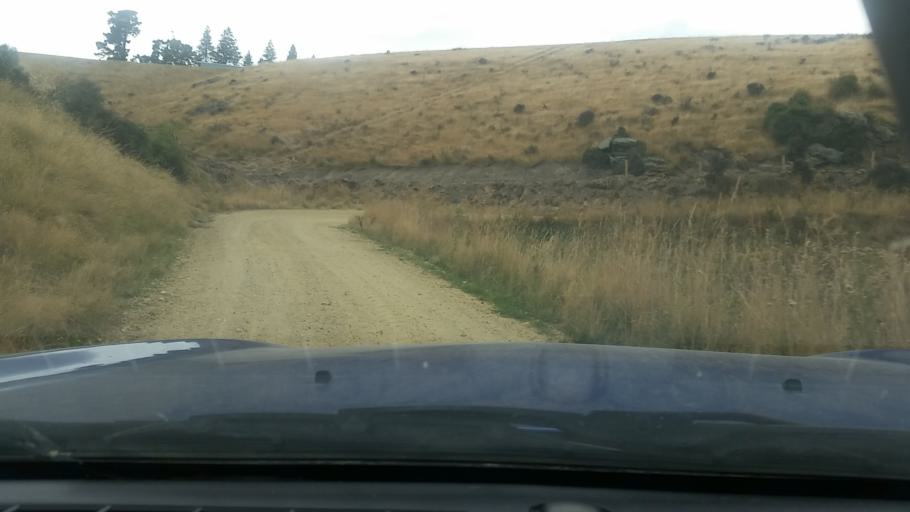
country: NZ
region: Southland
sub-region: Gore District
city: Gore
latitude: -45.5833
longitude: 169.3939
